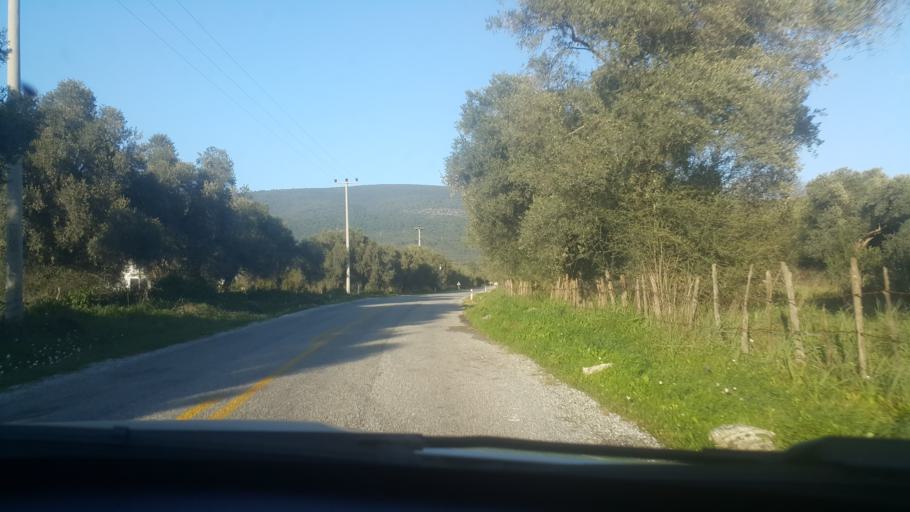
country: TR
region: Mugla
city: Kiulukioi
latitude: 37.2968
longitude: 27.5984
